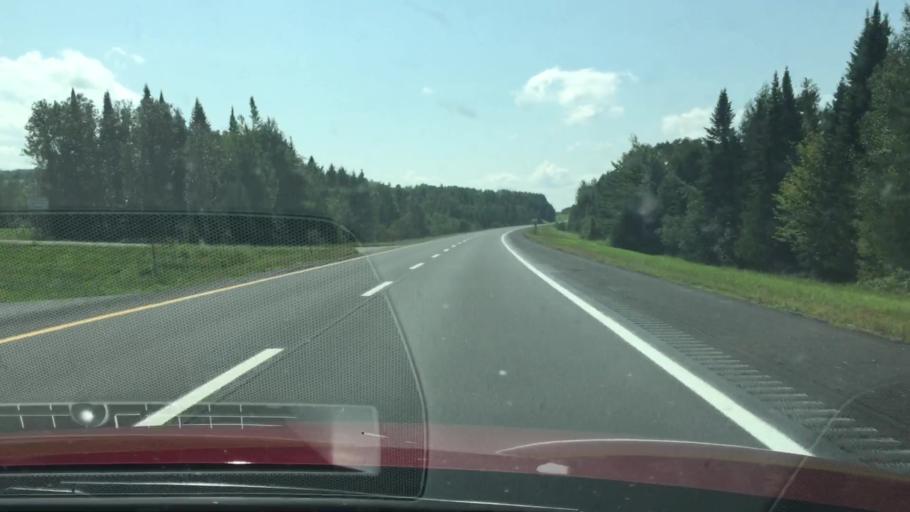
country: US
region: Maine
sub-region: Penobscot County
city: Patten
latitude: 45.9202
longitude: -68.3700
